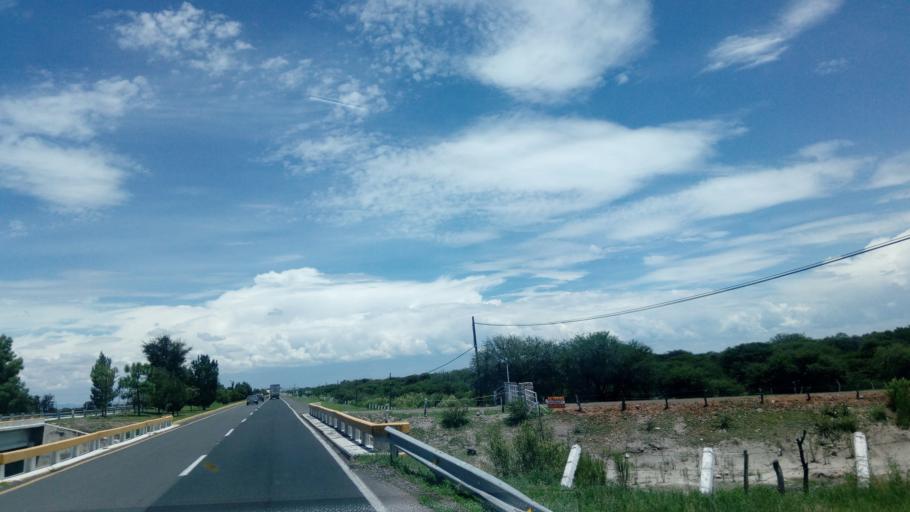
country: MX
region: Durango
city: Victoria de Durango
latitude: 24.1048
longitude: -104.5612
